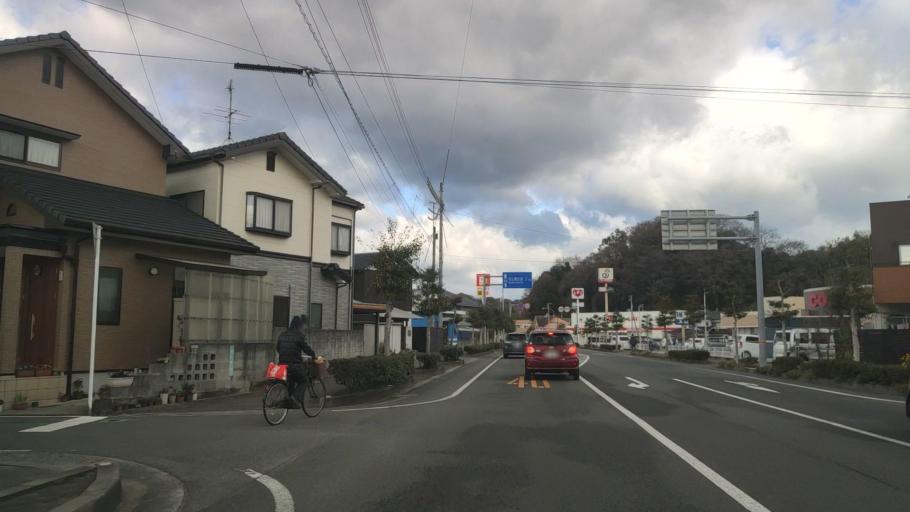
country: JP
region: Ehime
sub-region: Shikoku-chuo Shi
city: Matsuyama
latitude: 33.8668
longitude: 132.7249
